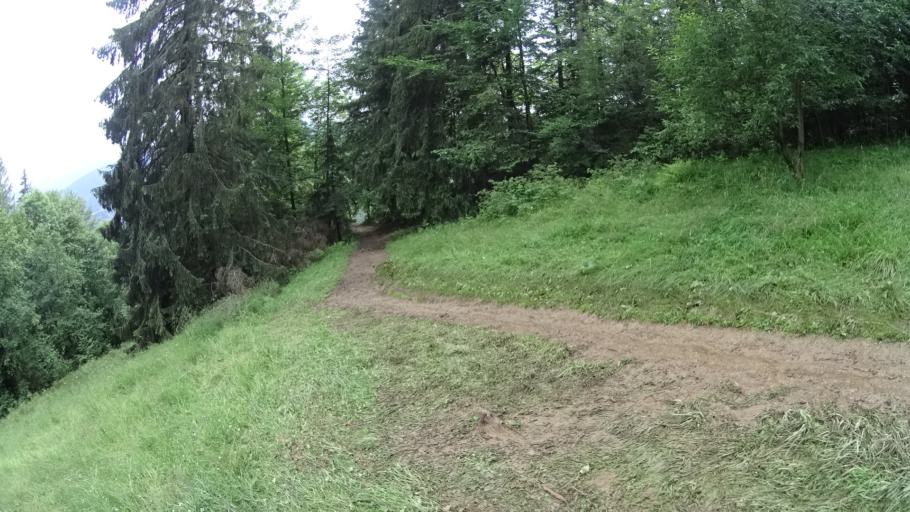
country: PL
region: Lesser Poland Voivodeship
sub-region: Powiat tatrzanski
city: Zakopane
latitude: 49.3039
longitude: 19.9426
